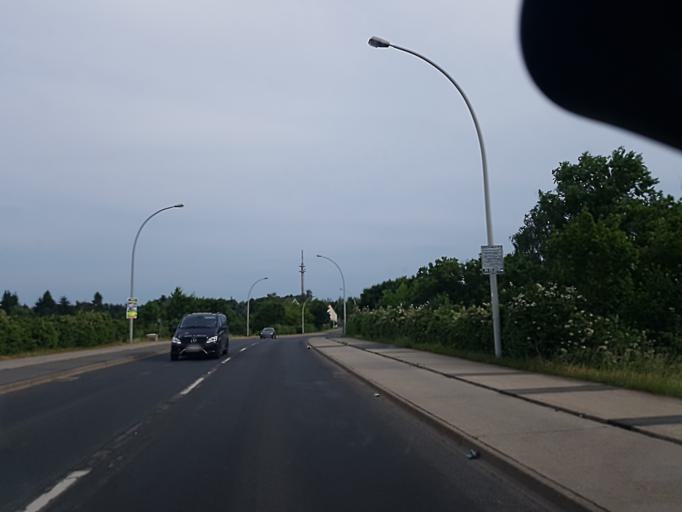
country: DE
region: Saxony-Anhalt
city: Wittenburg
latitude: 51.8739
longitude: 12.6697
